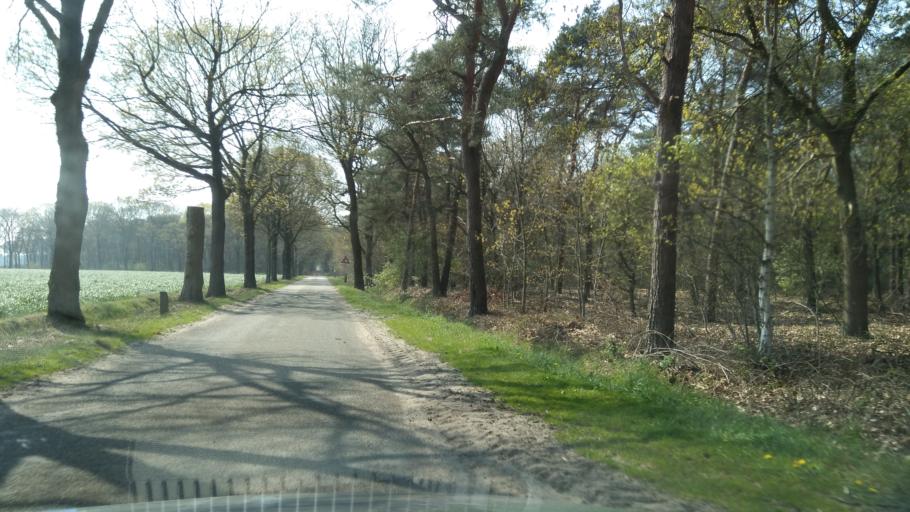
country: NL
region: North Brabant
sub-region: Gemeente Baarle-Nassau
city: Baarle-Nassau
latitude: 51.4222
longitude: 4.9254
